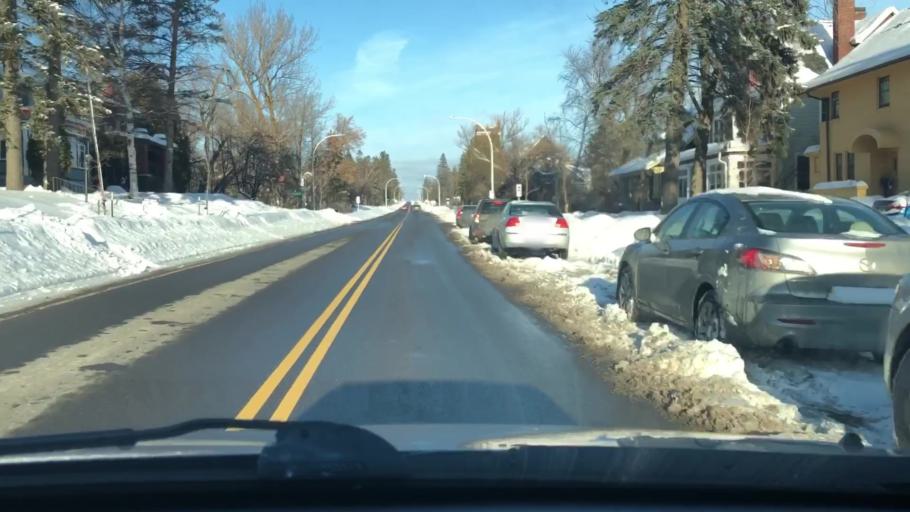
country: US
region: Minnesota
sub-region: Saint Louis County
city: Duluth
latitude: 46.8100
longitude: -92.0759
